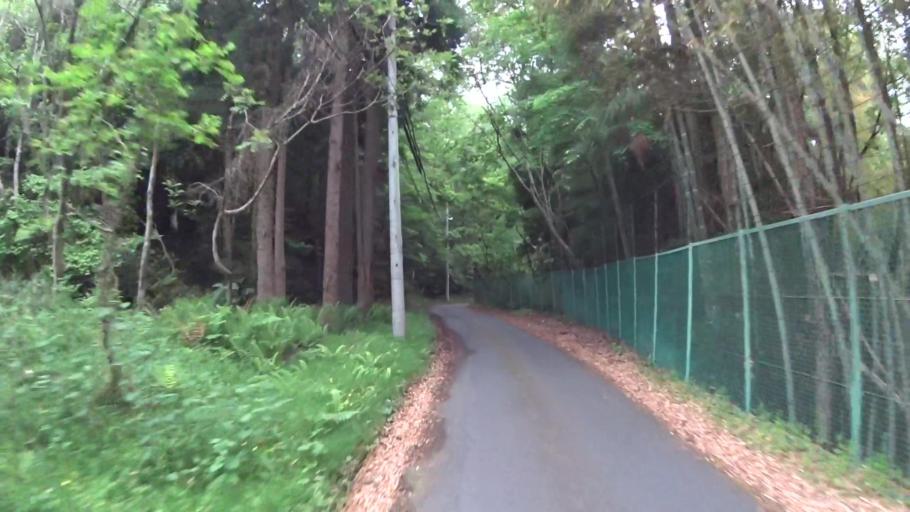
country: JP
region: Kyoto
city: Kameoka
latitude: 35.0623
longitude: 135.5348
